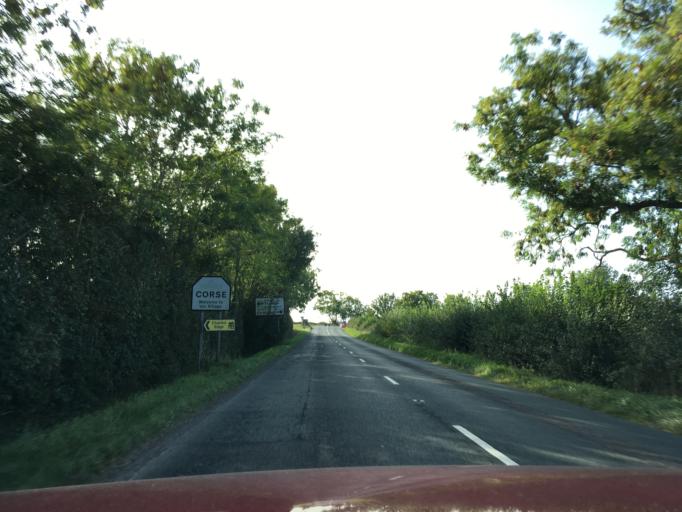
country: GB
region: England
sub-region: Gloucestershire
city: Gloucester
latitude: 51.9623
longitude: -2.2714
